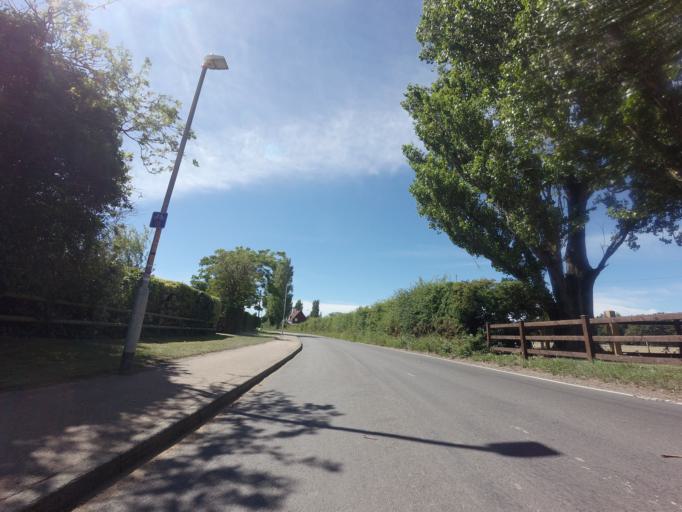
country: GB
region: England
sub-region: Kent
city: Sandwich
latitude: 51.2710
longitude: 1.3599
